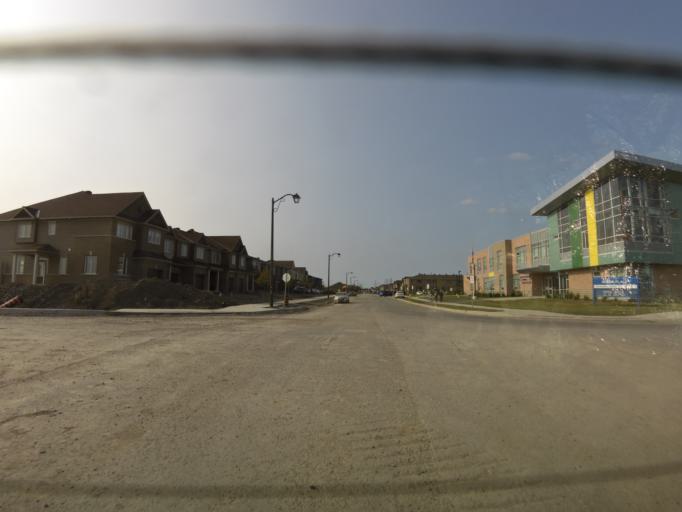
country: CA
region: Ontario
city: Ottawa
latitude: 45.4465
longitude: -75.4854
